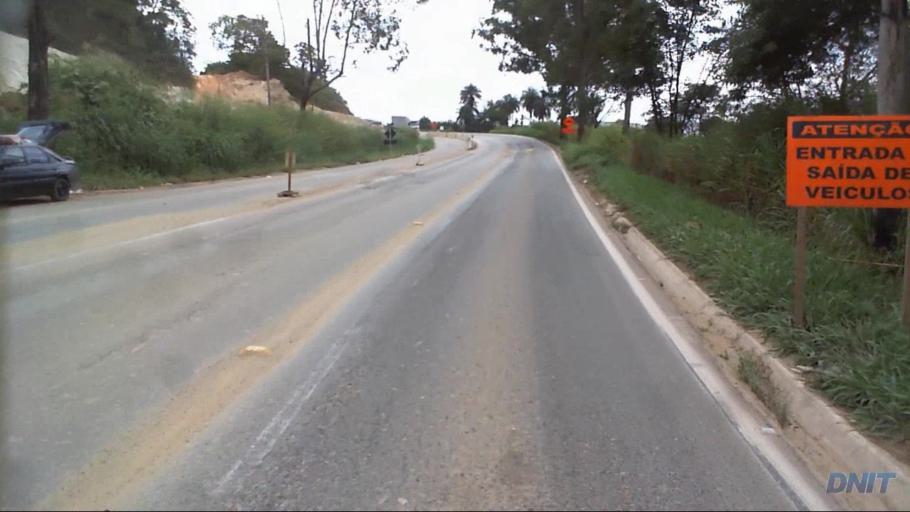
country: BR
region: Minas Gerais
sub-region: Caete
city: Caete
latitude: -19.7856
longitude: -43.6644
